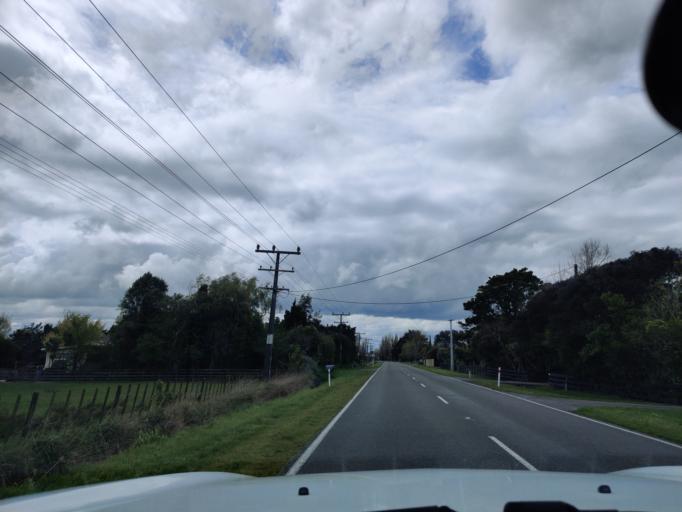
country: NZ
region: Manawatu-Wanganui
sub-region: Palmerston North City
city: Palmerston North
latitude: -40.2428
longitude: 175.5569
